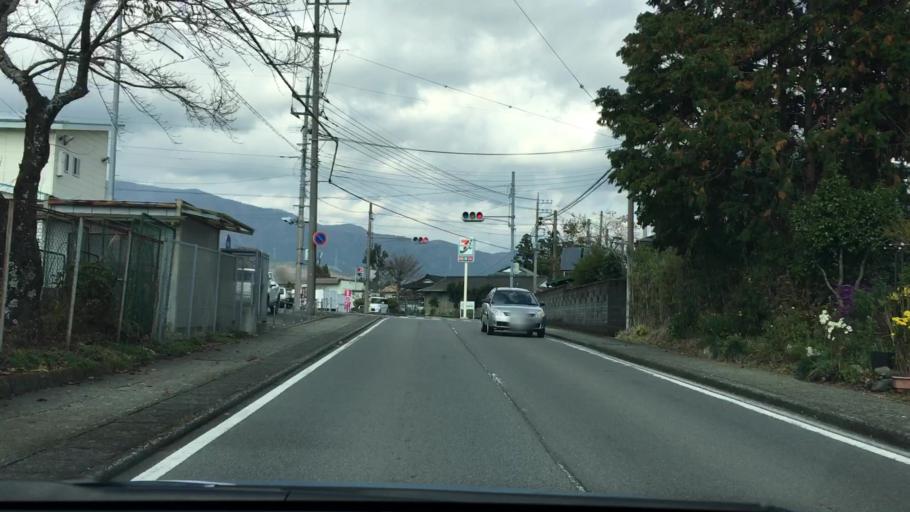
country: JP
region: Shizuoka
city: Gotemba
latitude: 35.3448
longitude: 138.9439
